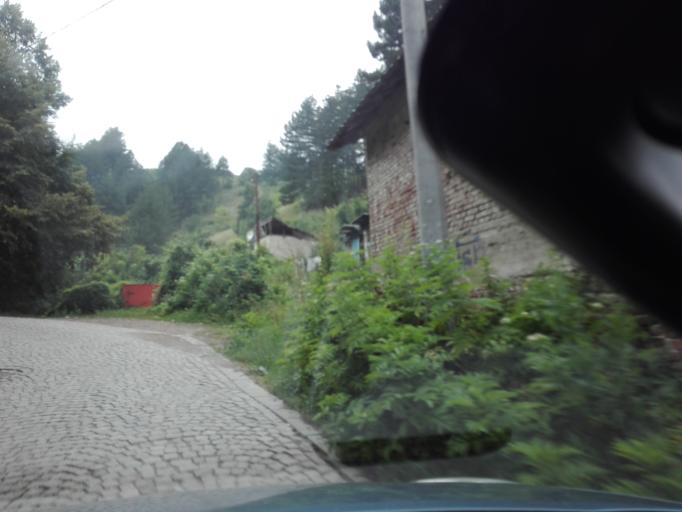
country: BG
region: Sofia-Capital
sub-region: Stolichna Obshtina
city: Sofia
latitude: 42.6072
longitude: 23.3971
